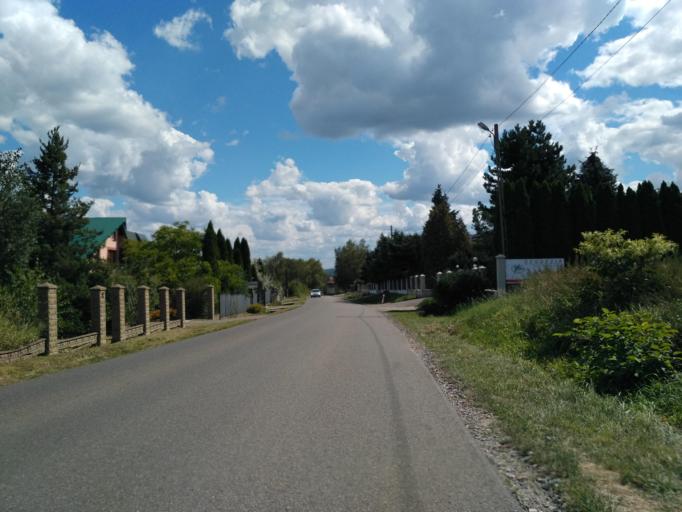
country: PL
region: Subcarpathian Voivodeship
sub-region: Powiat jasielski
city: Trzcinica
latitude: 49.7503
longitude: 21.4308
